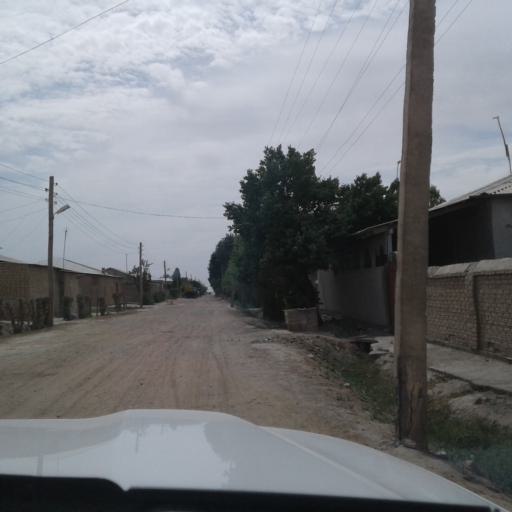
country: TM
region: Dasoguz
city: Tagta
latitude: 41.5996
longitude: 59.8511
